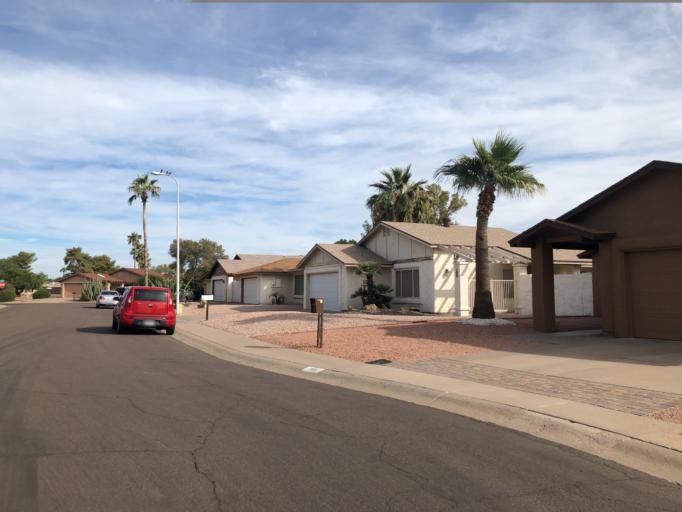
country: US
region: Arizona
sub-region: Maricopa County
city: Tempe
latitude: 33.4555
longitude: -111.8927
